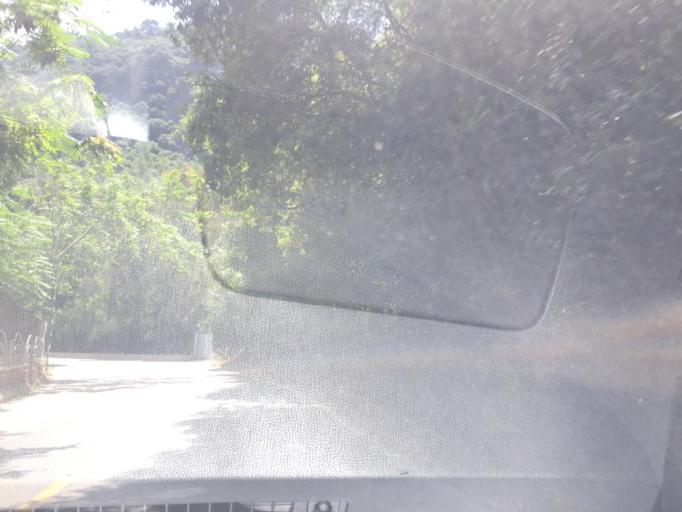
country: LB
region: Mont-Liban
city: Beit ed Dine
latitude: 33.6981
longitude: 35.4738
